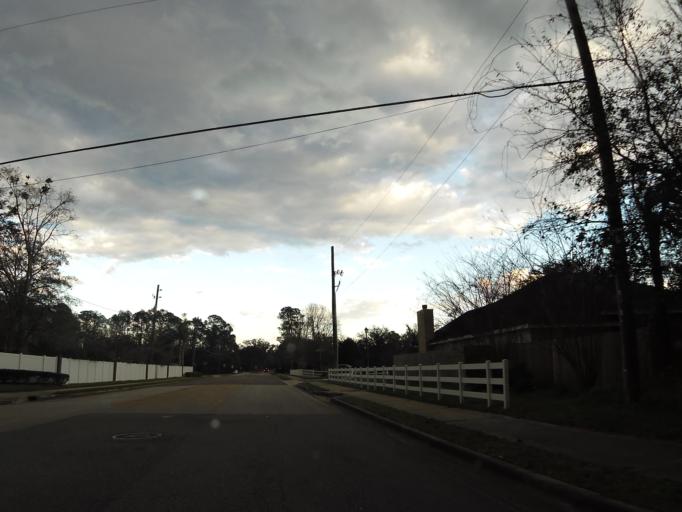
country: US
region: Florida
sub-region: Saint Johns County
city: Fruit Cove
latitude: 30.1724
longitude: -81.5718
